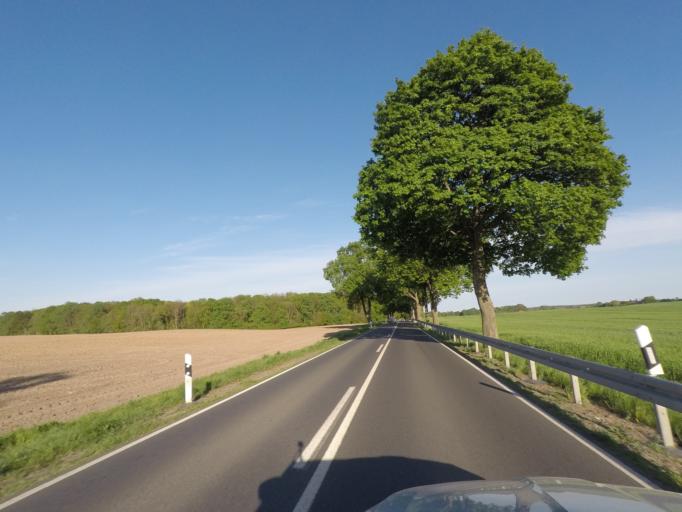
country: DE
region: Brandenburg
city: Hohenfinow
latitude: 52.8157
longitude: 13.9074
